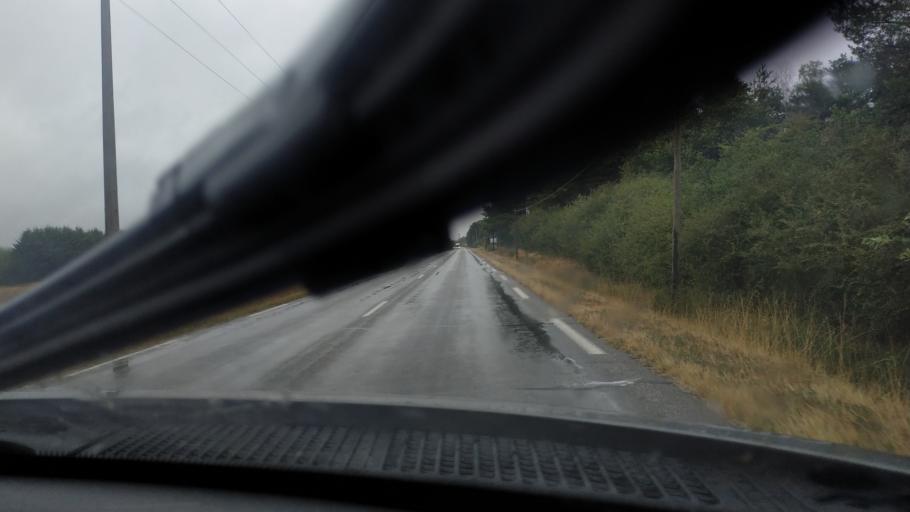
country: FR
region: Centre
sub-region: Departement du Loiret
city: Bellegarde
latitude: 47.9336
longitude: 2.3900
